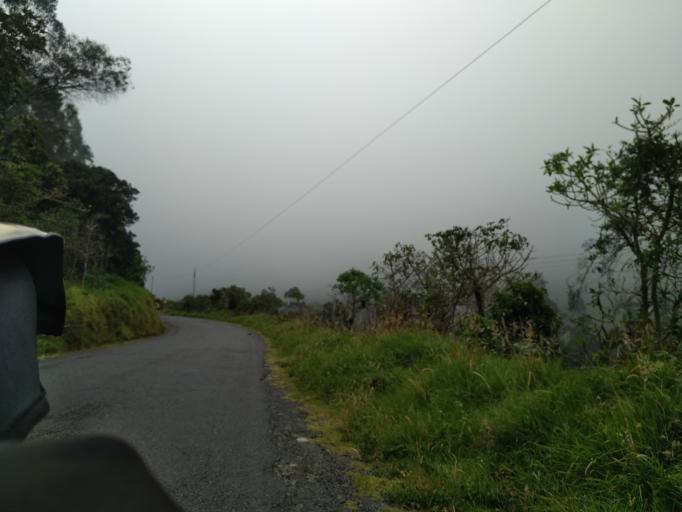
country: EC
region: Cotopaxi
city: Saquisili
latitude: -0.6951
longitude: -78.8146
